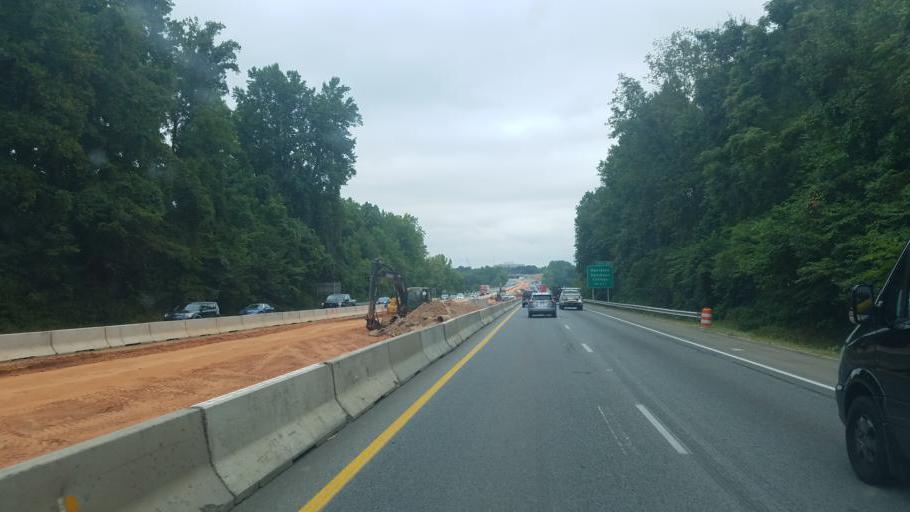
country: US
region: North Carolina
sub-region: Mecklenburg County
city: Cornelius
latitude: 35.4943
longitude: -80.8706
